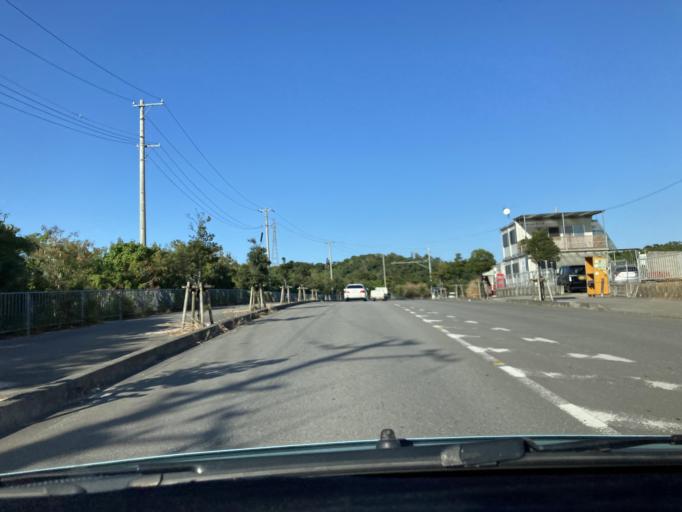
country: JP
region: Okinawa
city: Gushikawa
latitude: 26.3853
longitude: 127.8397
